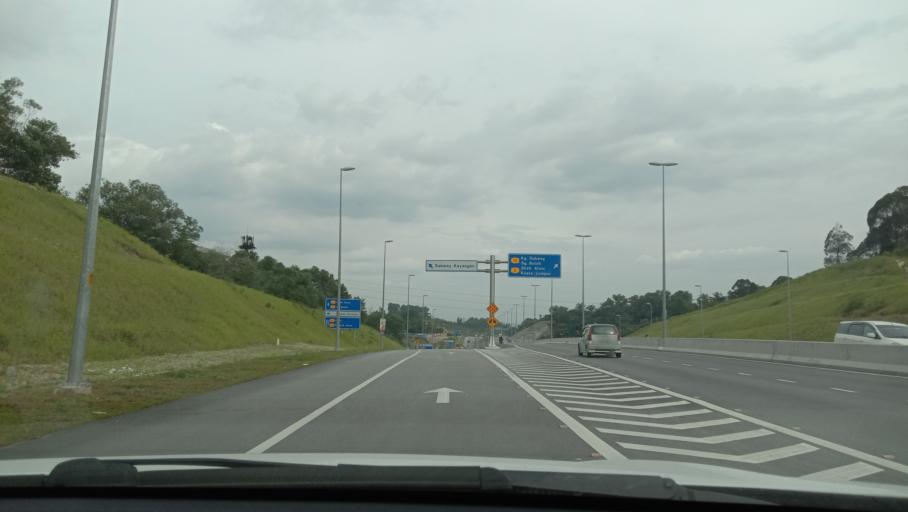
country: MY
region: Selangor
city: Kampung Baru Subang
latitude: 3.1266
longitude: 101.5166
